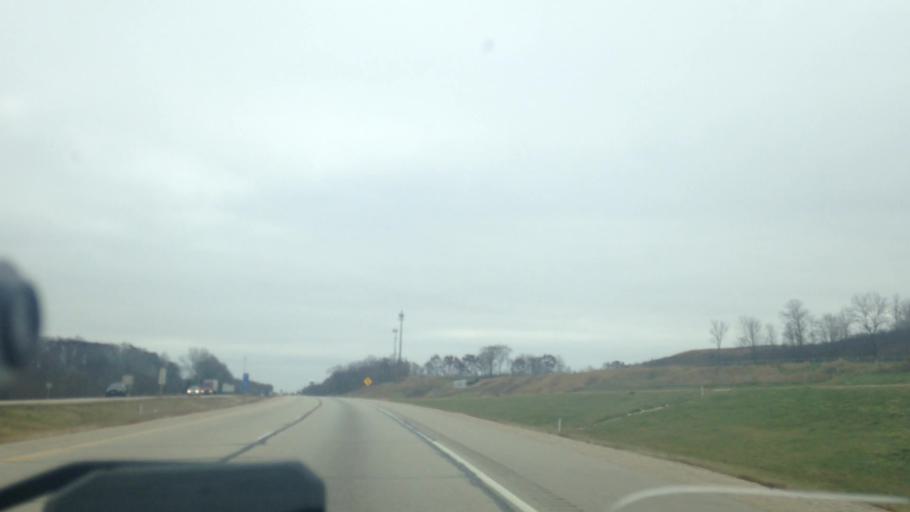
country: US
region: Wisconsin
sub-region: Washington County
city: Slinger
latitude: 43.3467
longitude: -88.2815
